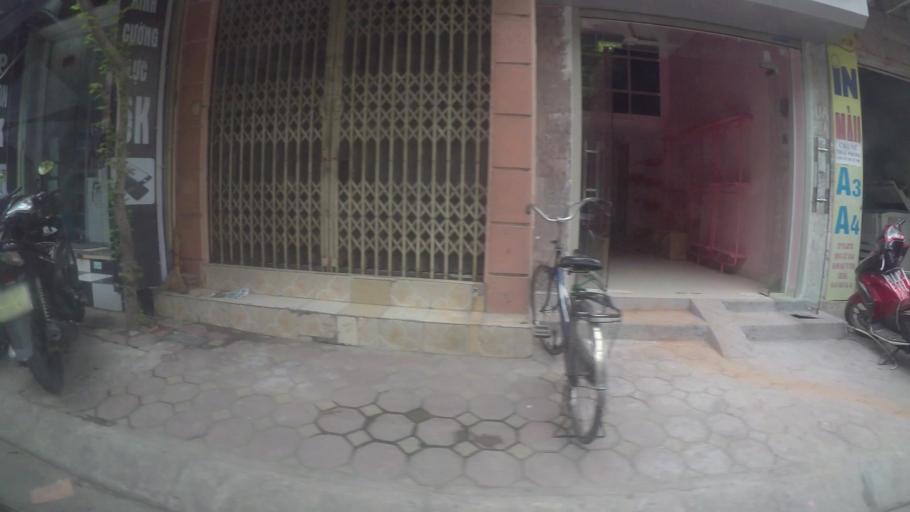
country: VN
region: Ha Noi
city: Cau Dien
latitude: 21.0409
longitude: 105.7747
